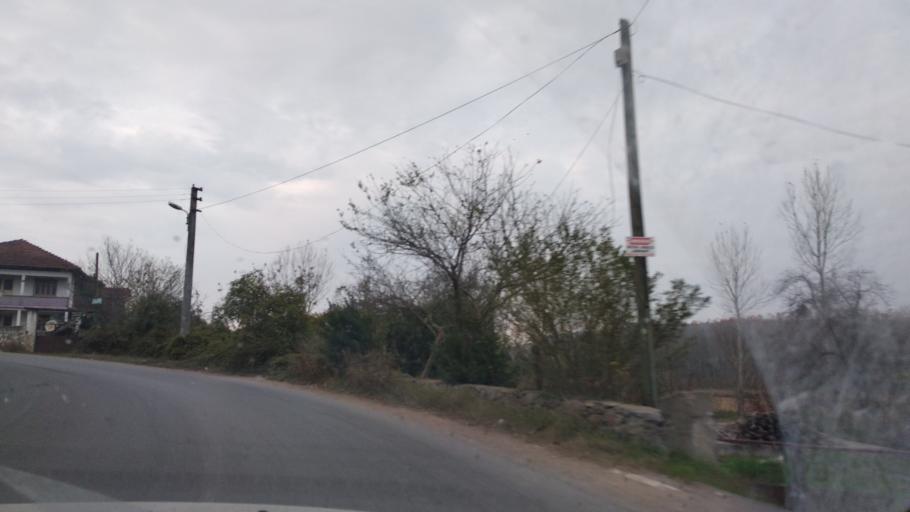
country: TR
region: Sakarya
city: Ortakoy
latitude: 41.0389
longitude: 30.6432
